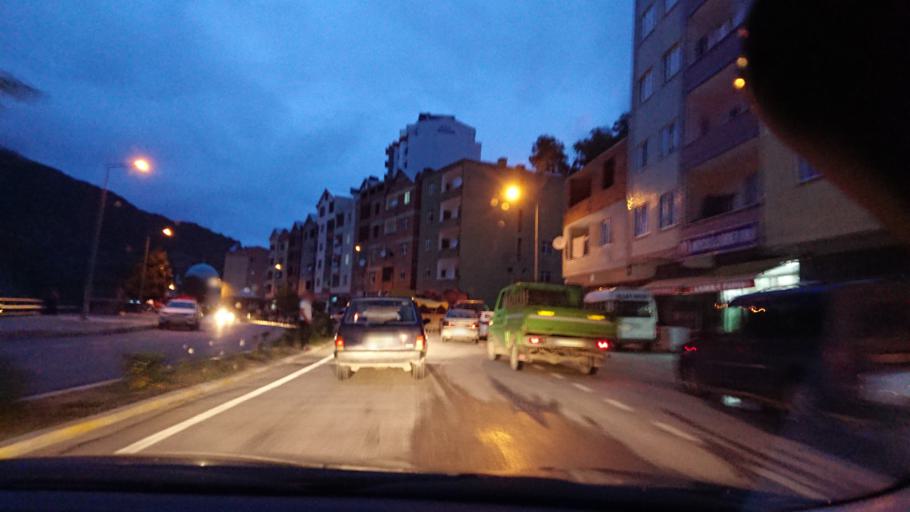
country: TR
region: Gumushane
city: Kurtun
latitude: 40.6683
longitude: 39.1414
